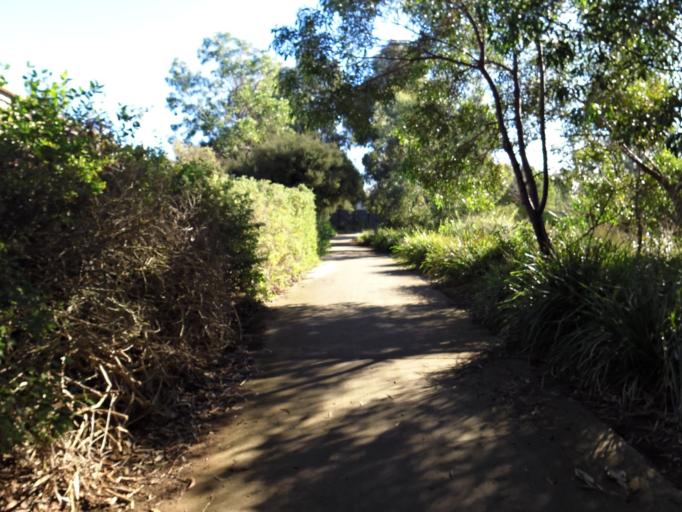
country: AU
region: Victoria
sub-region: Wyndham
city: Hoppers Crossing
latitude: -37.8449
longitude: 144.6997
